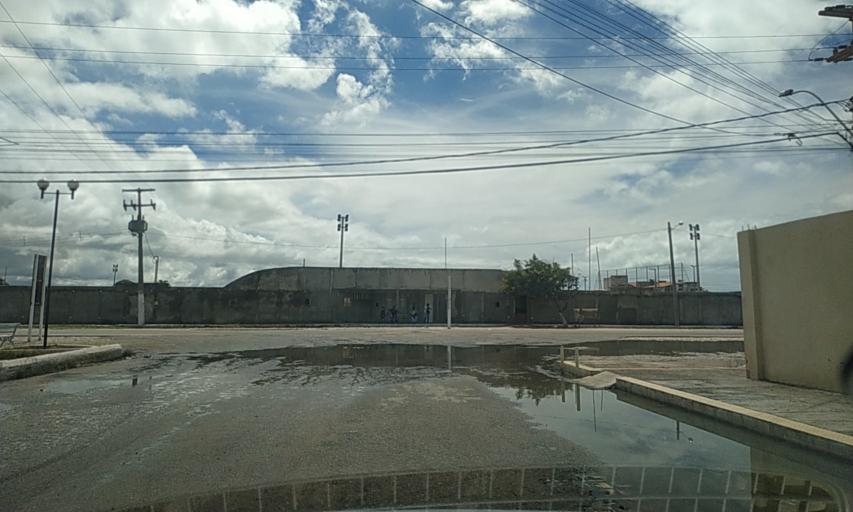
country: BR
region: Rio Grande do Norte
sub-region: Areia Branca
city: Areia Branca
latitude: -4.9532
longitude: -37.1281
